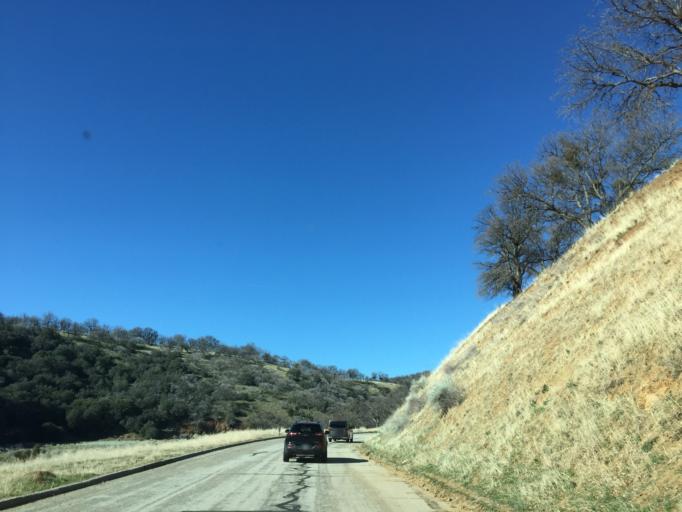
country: US
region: California
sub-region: Kern County
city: Lebec
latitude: 34.8837
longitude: -118.7775
